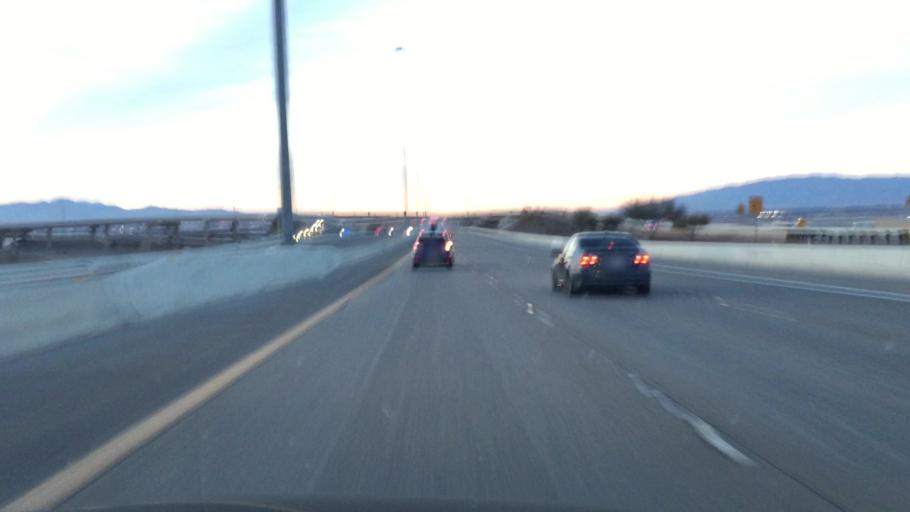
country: US
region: Nevada
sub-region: Clark County
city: Henderson
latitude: 36.0306
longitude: -115.0110
